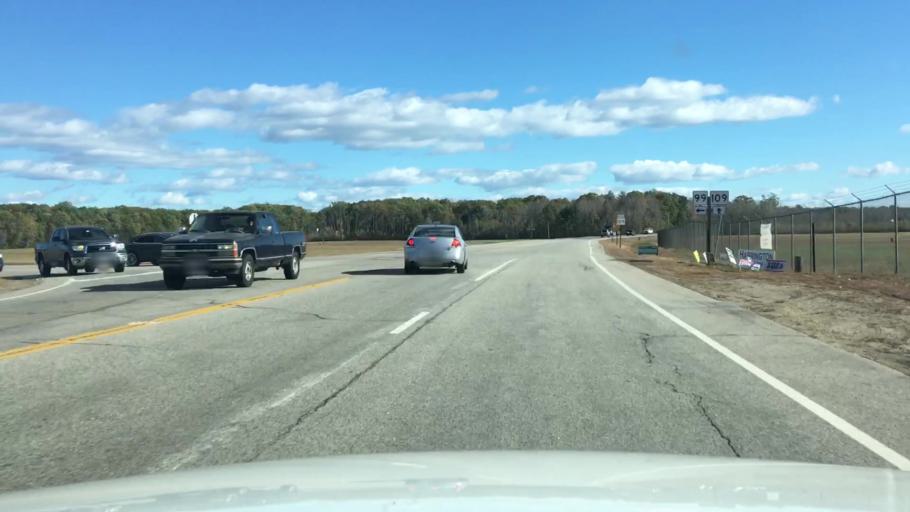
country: US
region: Maine
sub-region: York County
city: South Sanford
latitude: 43.3977
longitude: -70.6979
